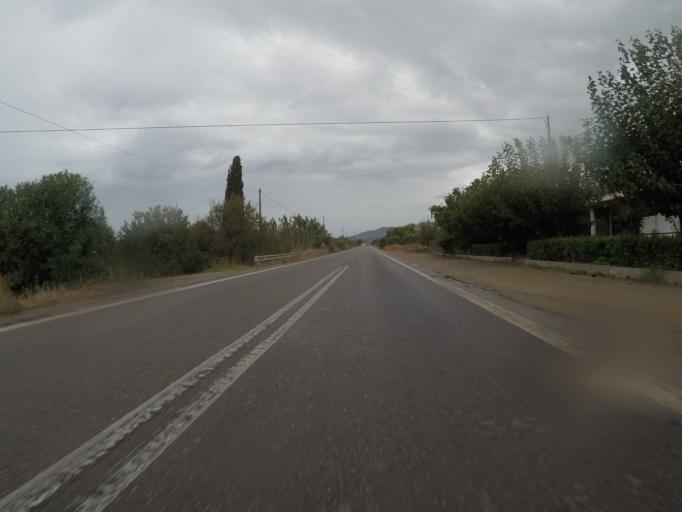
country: GR
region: West Greece
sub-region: Nomos Ileias
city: Zacharo
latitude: 37.4302
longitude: 21.6652
